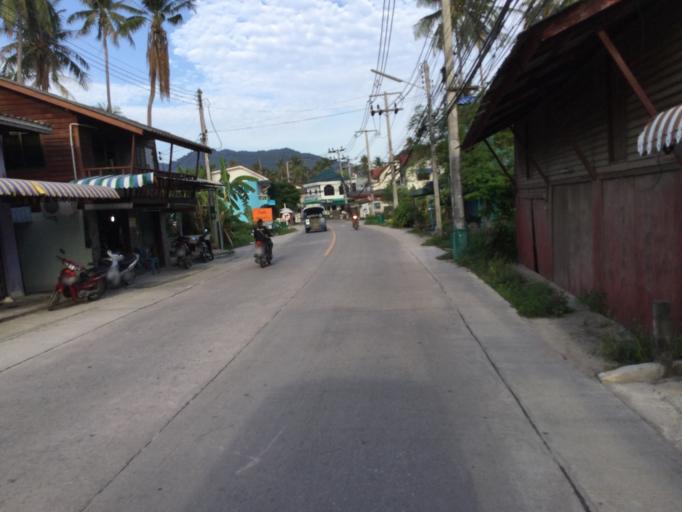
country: TH
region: Surat Thani
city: Ko Pha-Ngan
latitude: 9.7002
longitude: 100.0208
